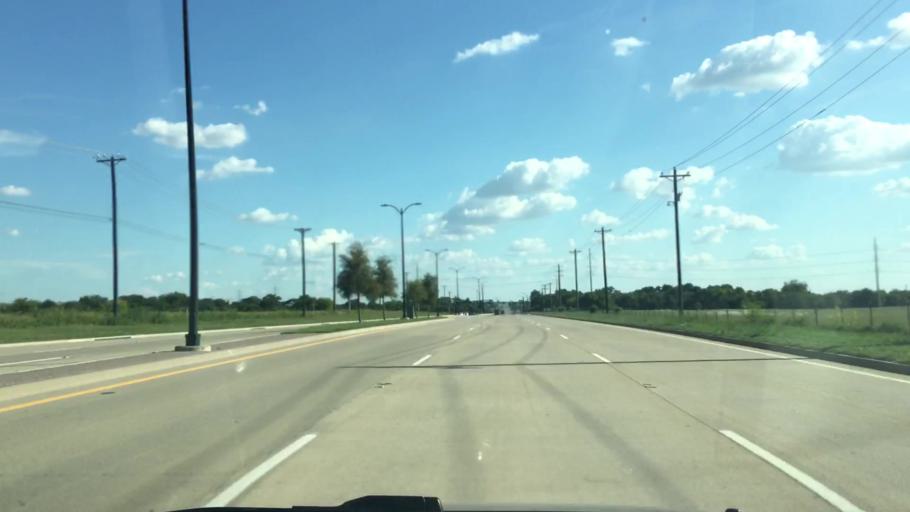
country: US
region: Texas
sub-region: Collin County
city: Prosper
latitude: 33.1938
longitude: -96.8029
